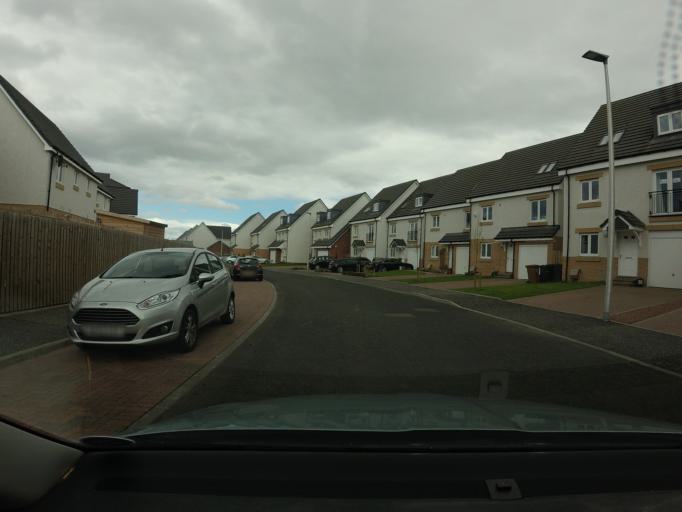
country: GB
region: Scotland
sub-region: Edinburgh
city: Kirkliston
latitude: 55.9529
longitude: -3.4080
